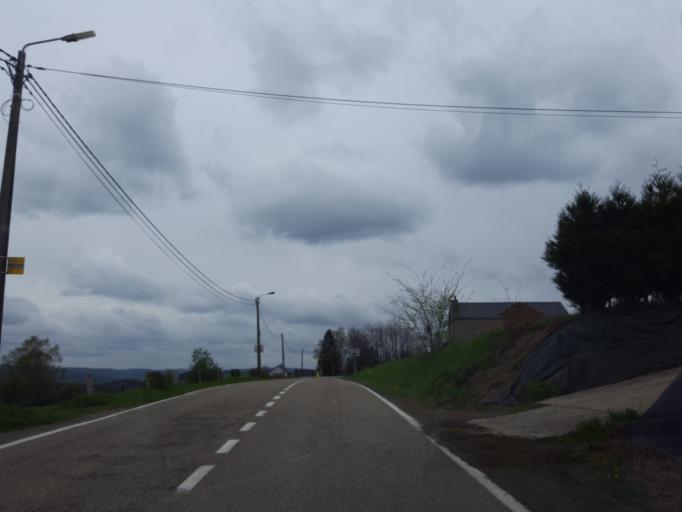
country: BE
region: Wallonia
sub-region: Province de Liege
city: Stoumont
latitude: 50.4061
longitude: 5.8140
